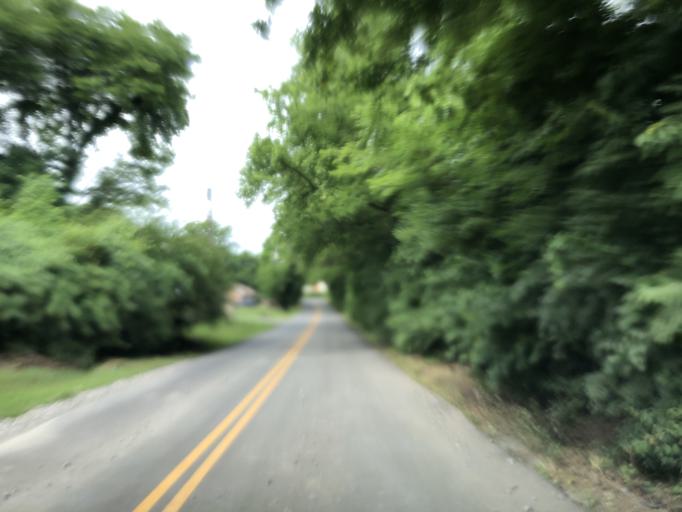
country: US
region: Tennessee
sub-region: Davidson County
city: Goodlettsville
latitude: 36.2794
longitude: -86.7055
